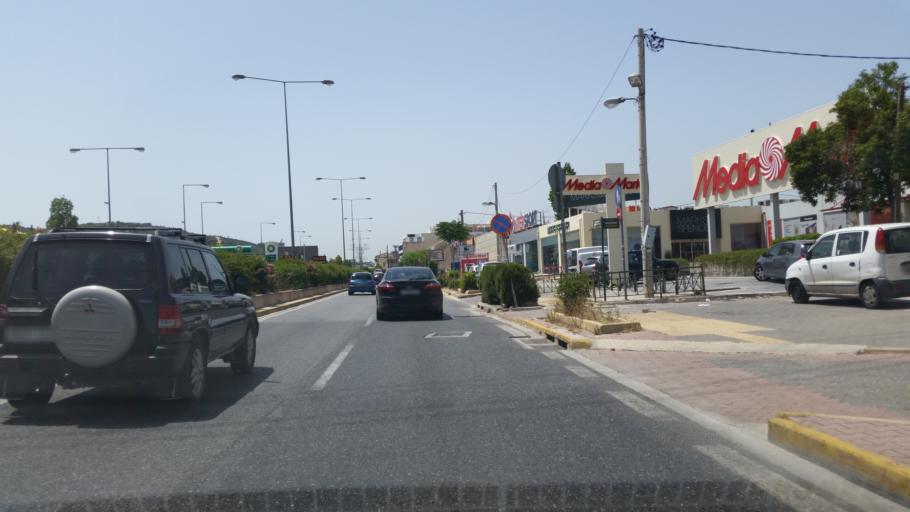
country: GR
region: Attica
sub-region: Nomarchia Anatolikis Attikis
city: Pallini
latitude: 38.0067
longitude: 23.8640
